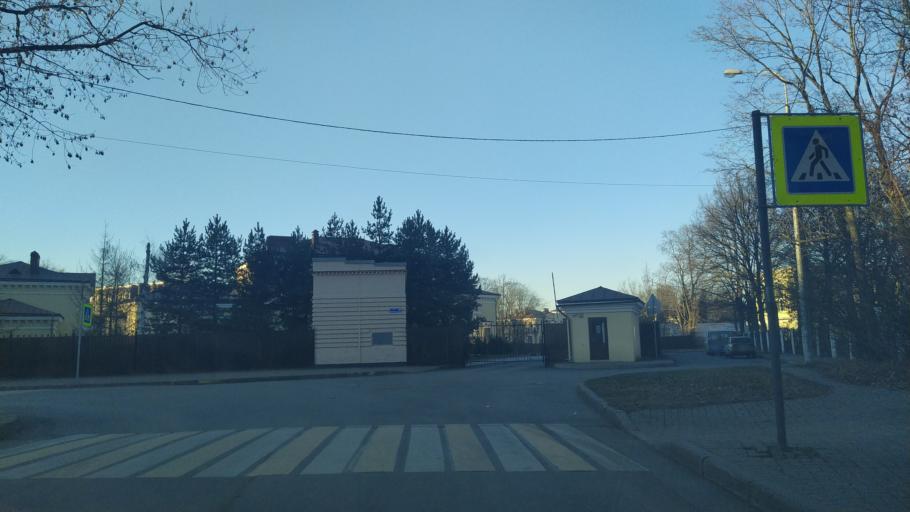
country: RU
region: St.-Petersburg
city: Novaya Derevnya
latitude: 59.9741
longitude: 30.2763
